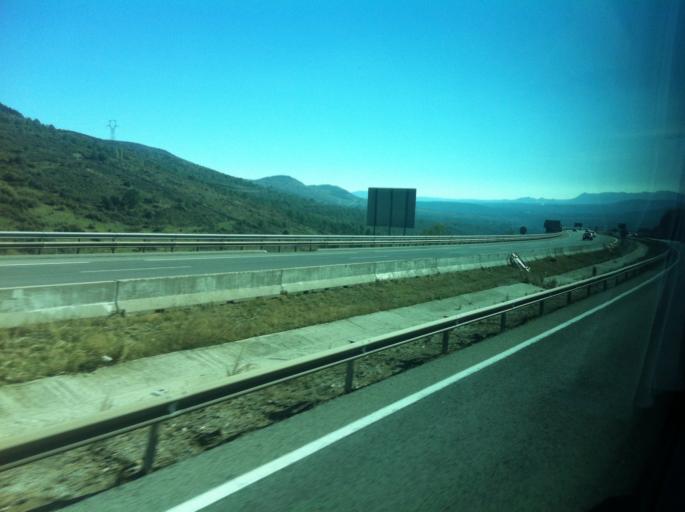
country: ES
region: Madrid
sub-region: Provincia de Madrid
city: Robregordo
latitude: 41.1126
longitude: -3.5879
